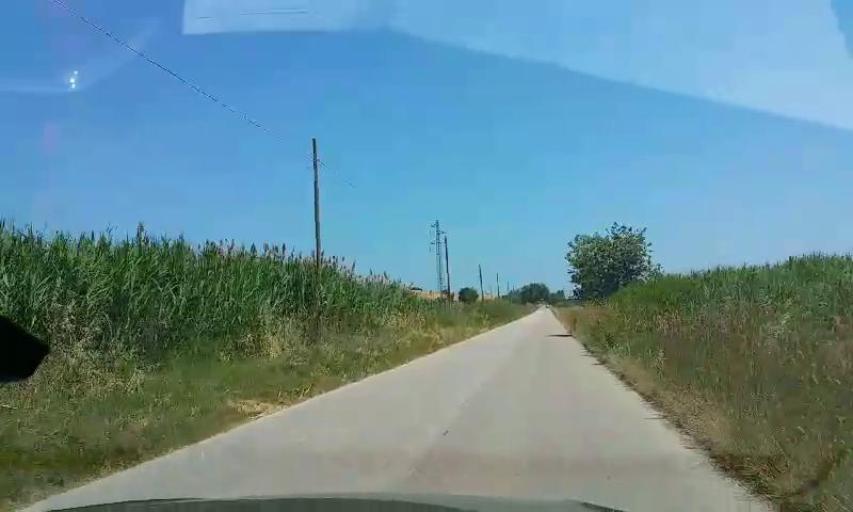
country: IT
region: Molise
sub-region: Provincia di Campobasso
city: San Giacomo degli Schiavoni
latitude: 41.9928
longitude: 14.9467
